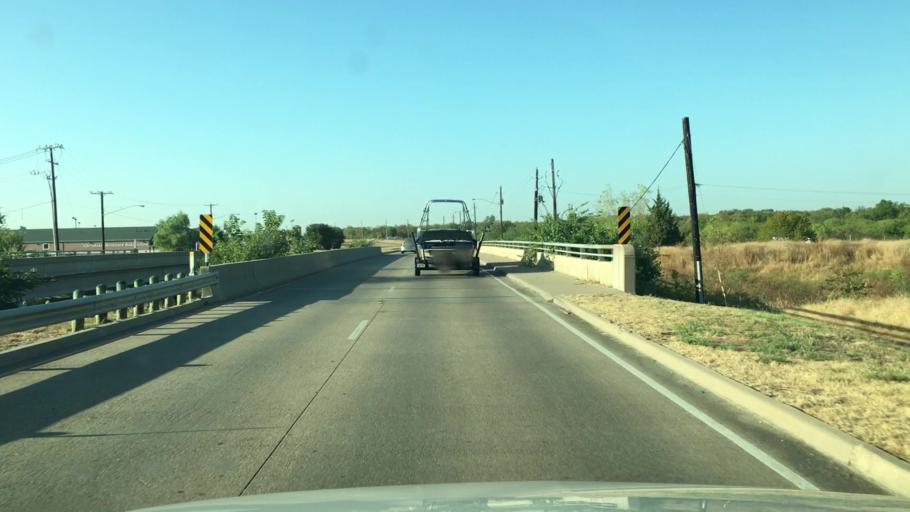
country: US
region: Texas
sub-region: Johnson County
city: Burleson
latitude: 32.5289
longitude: -97.3527
